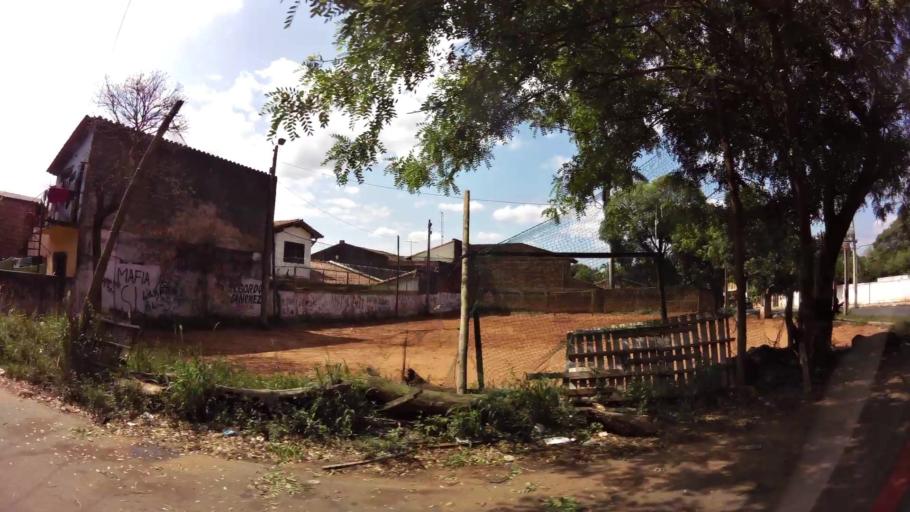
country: PY
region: Central
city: San Lorenzo
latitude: -25.3398
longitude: -57.5008
